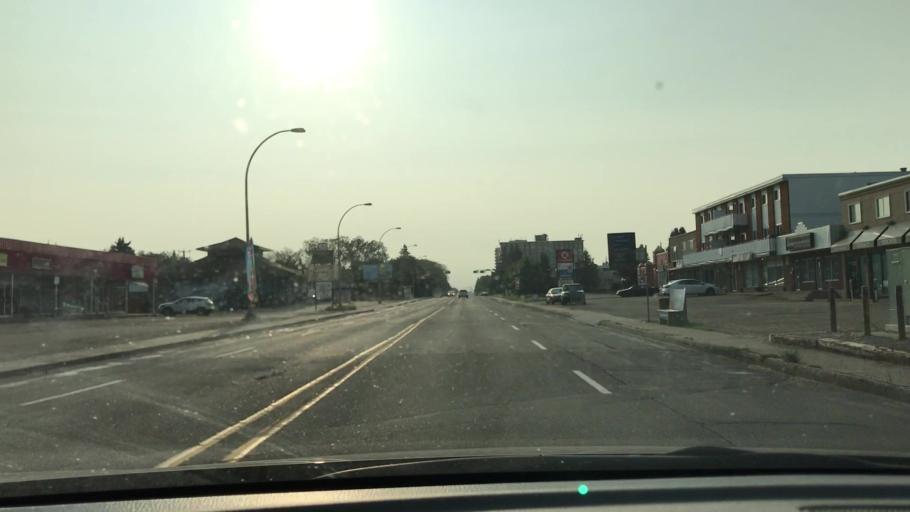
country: CA
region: Alberta
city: Edmonton
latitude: 53.5412
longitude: -113.4397
